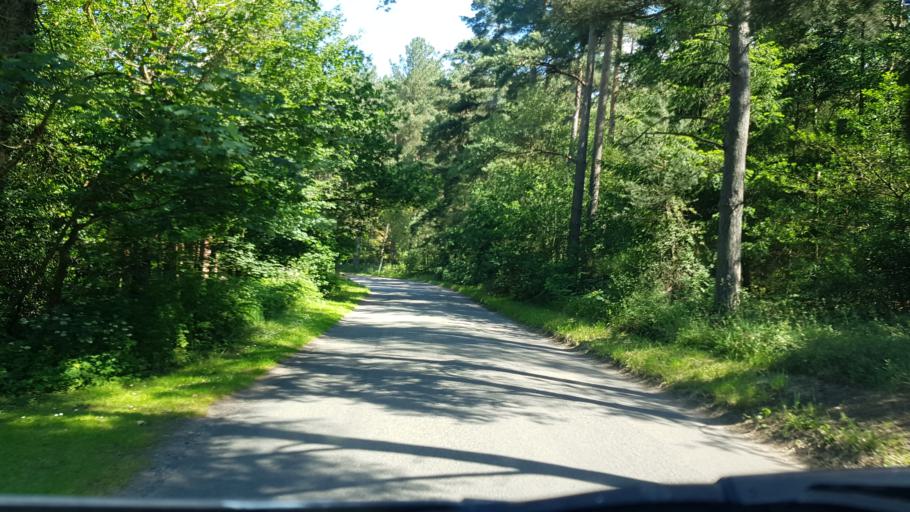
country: GB
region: England
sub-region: Worcestershire
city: Kidderminster
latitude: 52.4301
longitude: -2.2620
